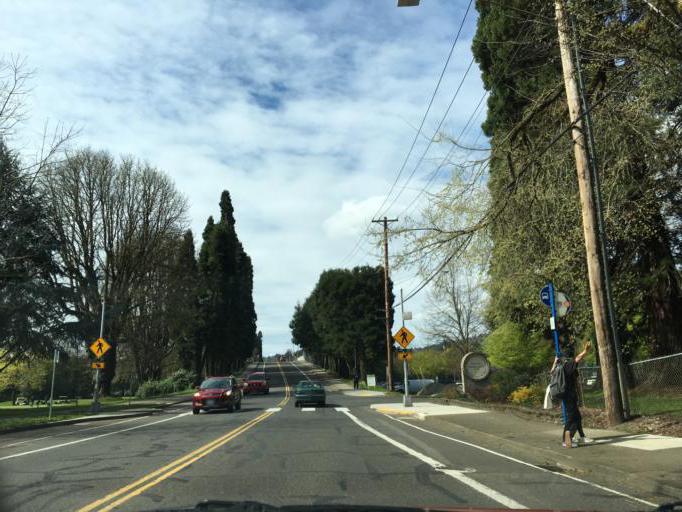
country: US
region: Oregon
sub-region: Clackamas County
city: Milwaukie
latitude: 45.4744
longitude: -122.6371
